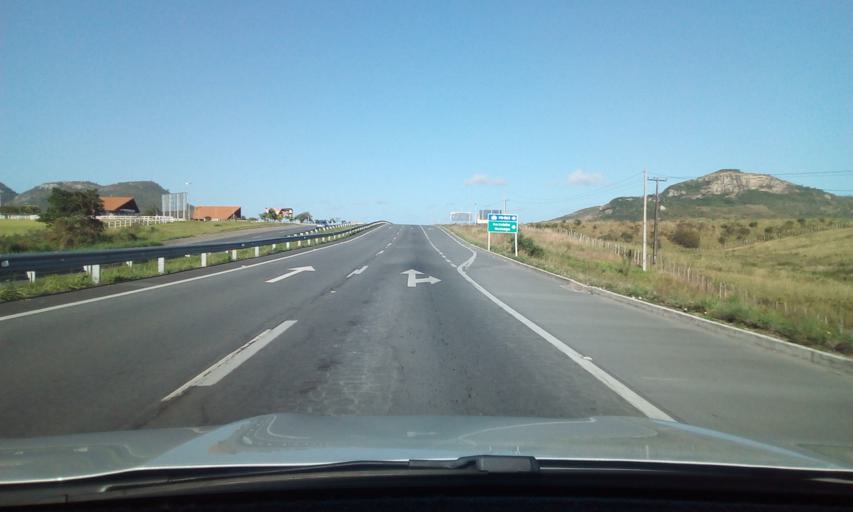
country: BR
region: Paraiba
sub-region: Gurinhem
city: Gurinhem
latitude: -7.1704
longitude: -35.3813
